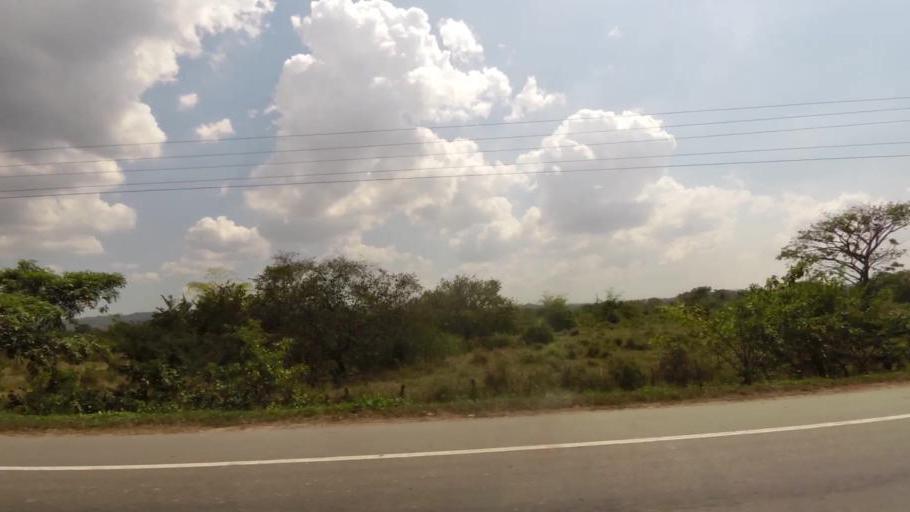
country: CO
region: Bolivar
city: Cartagena
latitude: 10.3547
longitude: -75.4758
